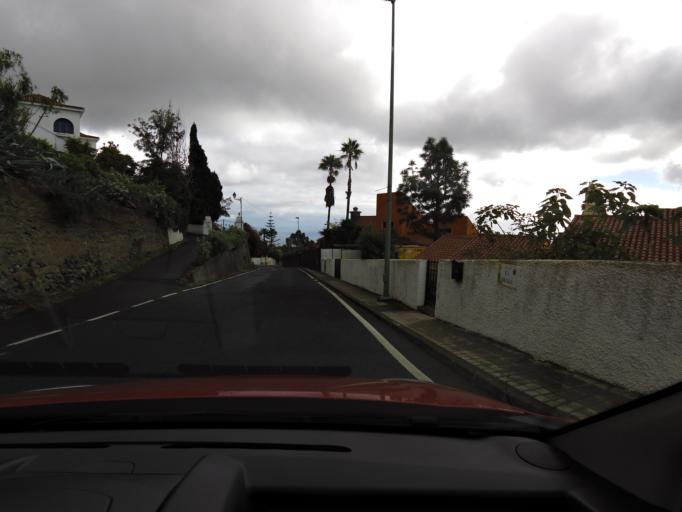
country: ES
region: Canary Islands
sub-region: Provincia de Las Palmas
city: Santa Brigida
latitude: 28.0319
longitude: -15.4691
